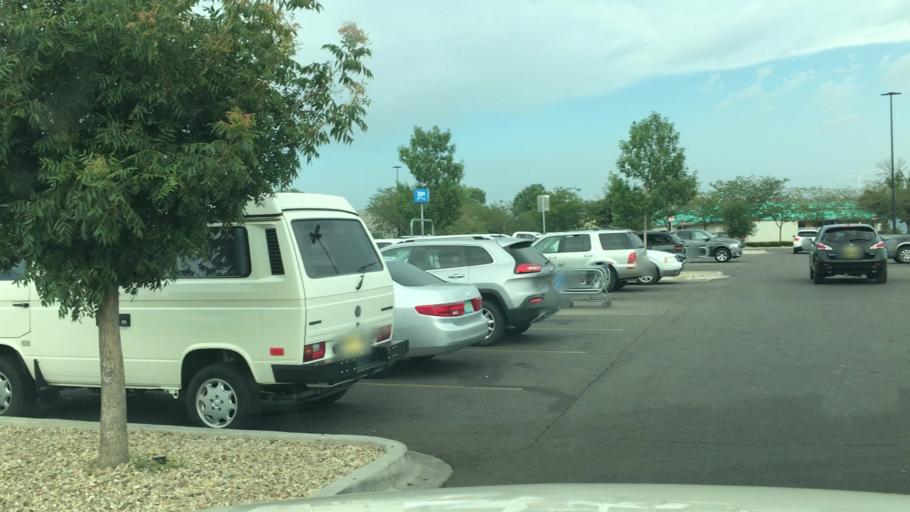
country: US
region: New Mexico
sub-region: Santa Fe County
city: Agua Fria
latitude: 35.6525
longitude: -105.9988
